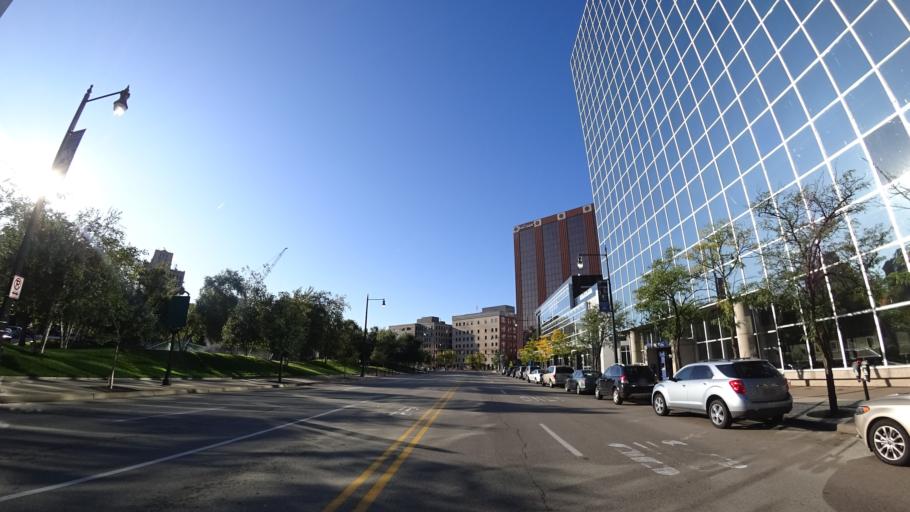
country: US
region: Michigan
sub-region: Kent County
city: Grand Rapids
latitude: 42.9661
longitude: -85.6722
